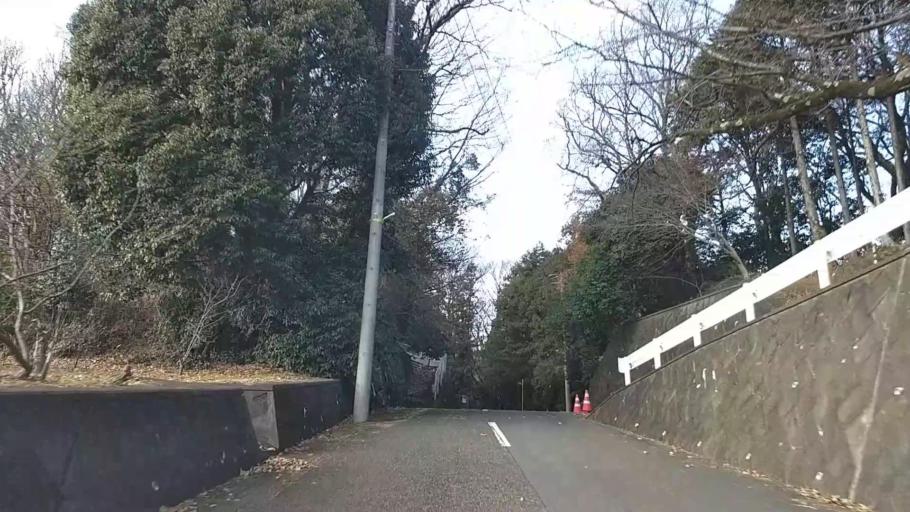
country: JP
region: Kanagawa
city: Isehara
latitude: 35.4299
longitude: 139.3145
